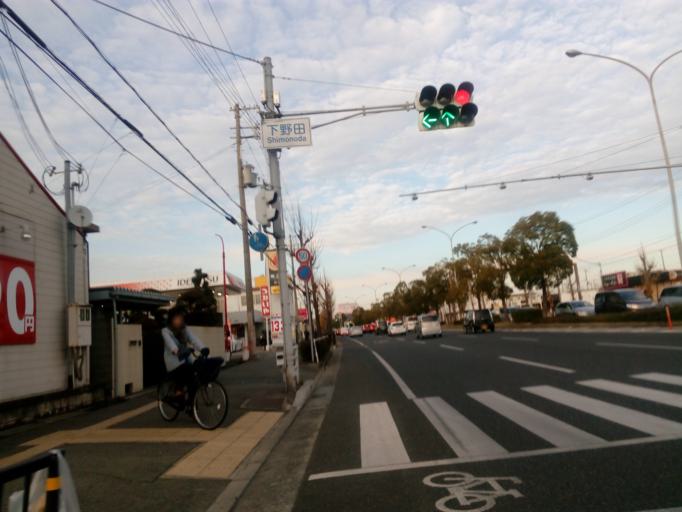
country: JP
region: Hyogo
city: Himeji
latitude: 34.8010
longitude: 134.6791
